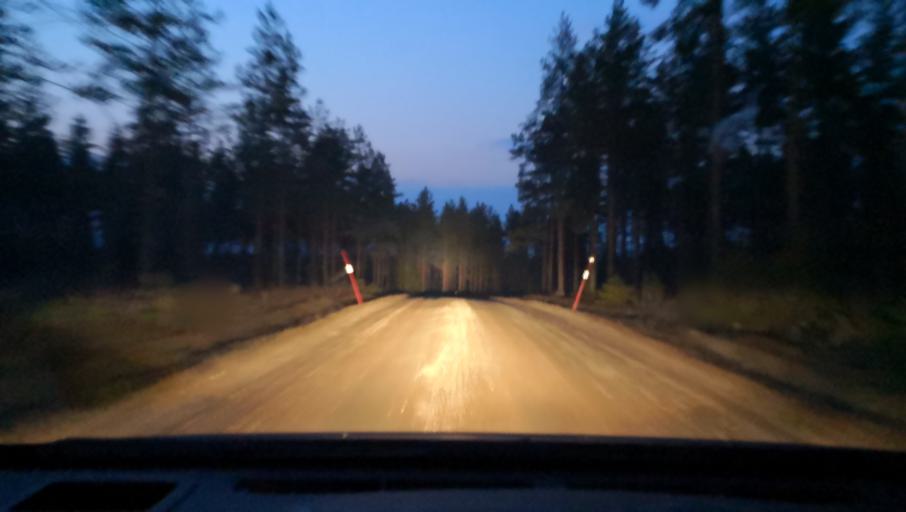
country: SE
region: OErebro
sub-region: Lindesbergs Kommun
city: Frovi
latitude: 59.6075
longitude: 15.4776
